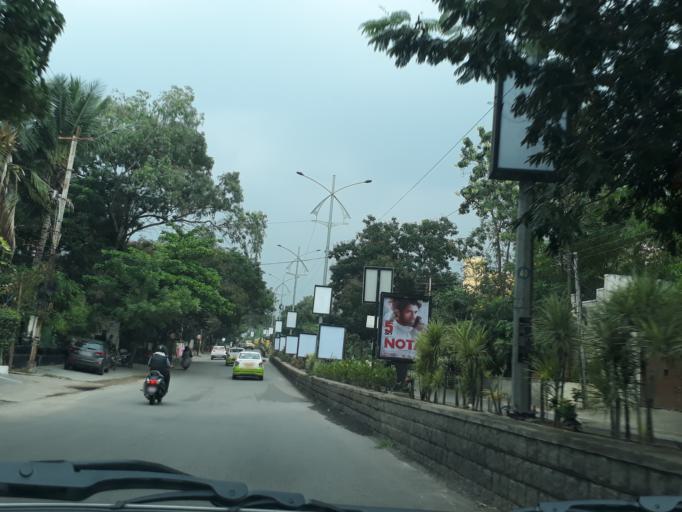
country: IN
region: Telangana
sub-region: Rangareddi
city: Kukatpalli
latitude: 17.4326
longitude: 78.4175
